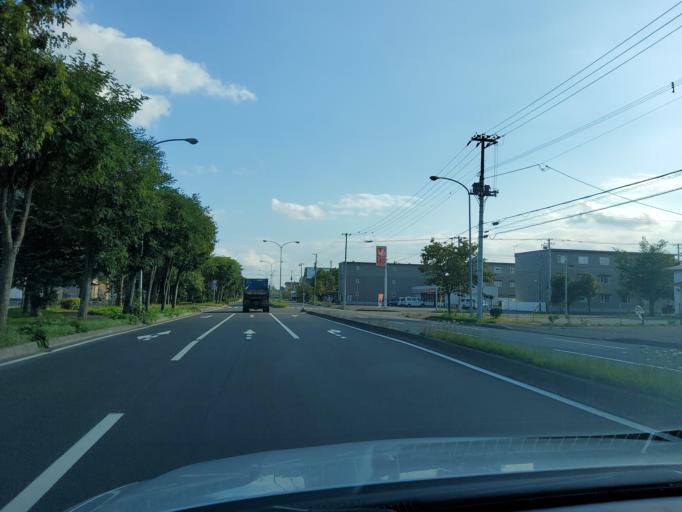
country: JP
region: Hokkaido
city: Obihiro
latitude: 42.9063
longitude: 143.2139
